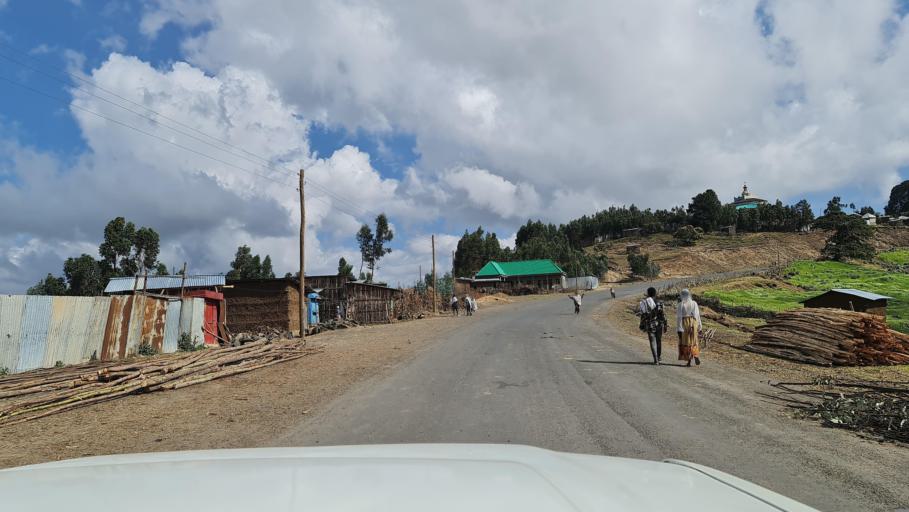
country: ET
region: Amhara
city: Debark'
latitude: 13.1576
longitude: 37.9129
